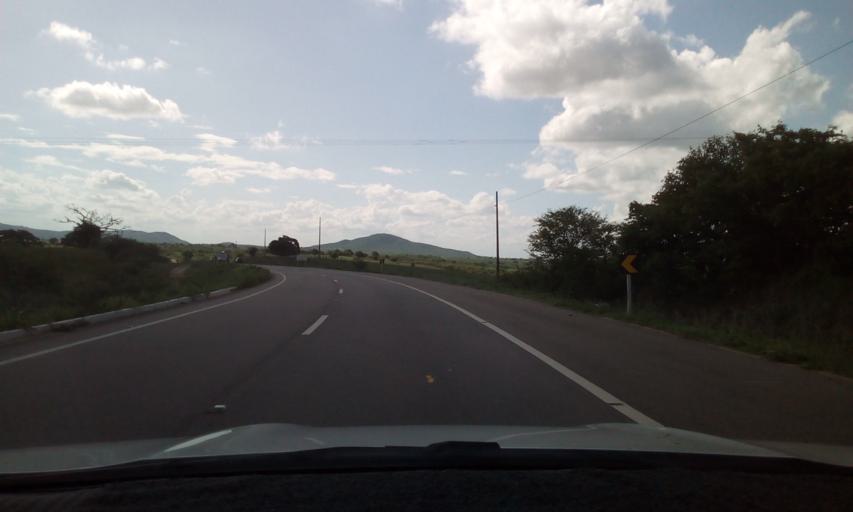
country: BR
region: Paraiba
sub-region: Gurinhem
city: Gurinhem
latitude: -7.1649
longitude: -35.3393
